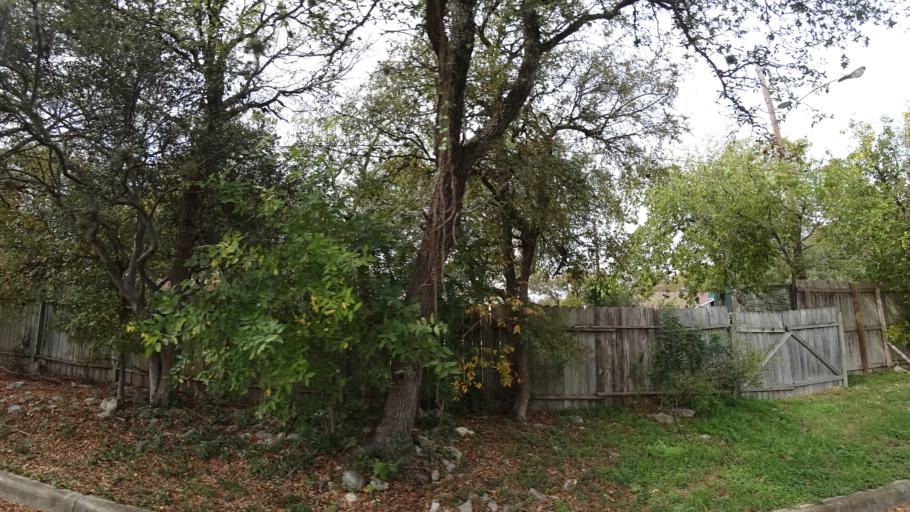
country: US
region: Texas
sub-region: Williamson County
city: Round Rock
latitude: 30.4966
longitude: -97.6934
